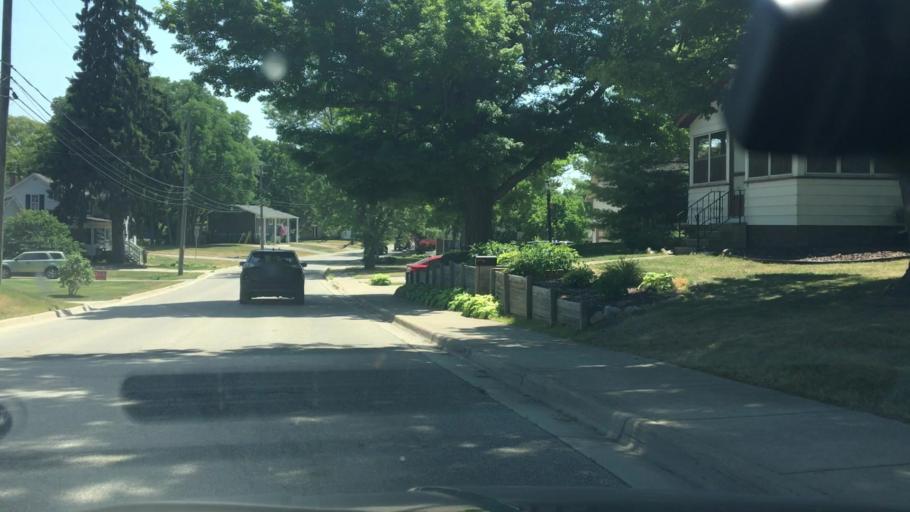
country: US
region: Michigan
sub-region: Livingston County
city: Brighton
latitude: 42.5272
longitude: -83.7762
